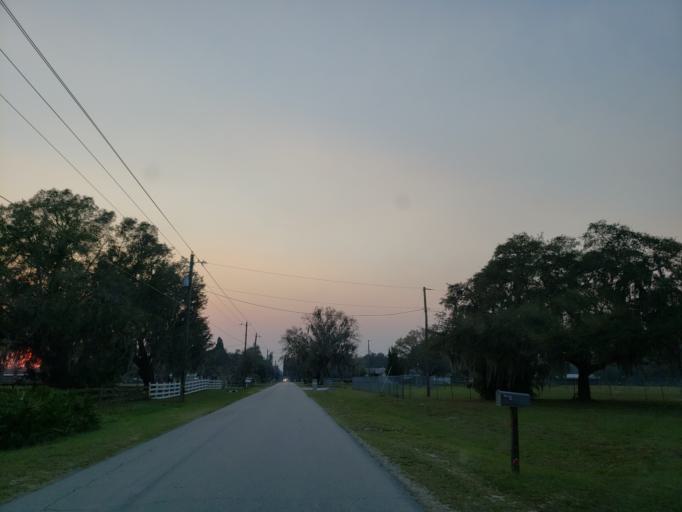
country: US
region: Florida
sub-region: Hillsborough County
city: Fish Hawk
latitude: 27.8428
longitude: -82.1894
